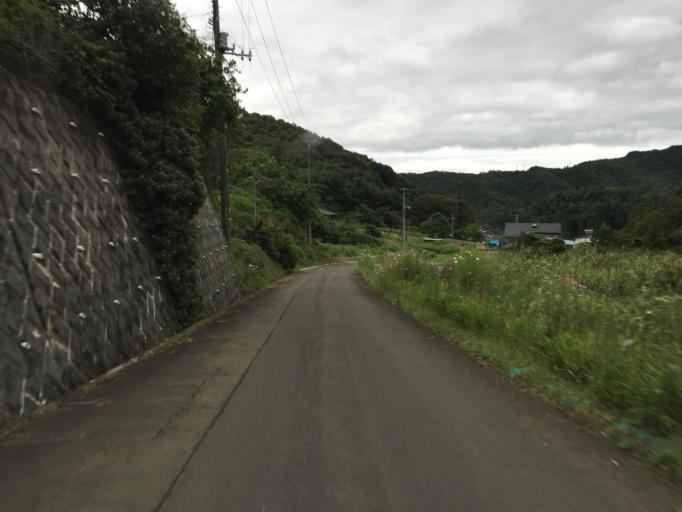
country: JP
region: Fukushima
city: Hobaramachi
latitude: 37.7612
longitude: 140.5396
